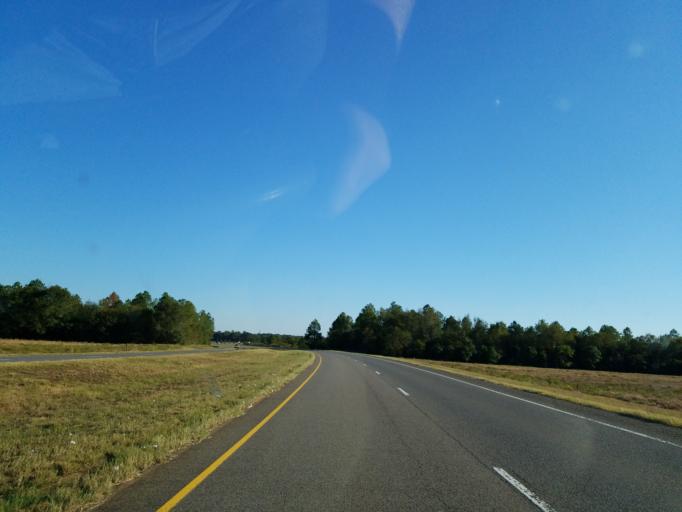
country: US
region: Georgia
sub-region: Lee County
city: Leesburg
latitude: 31.7284
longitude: -84.1825
